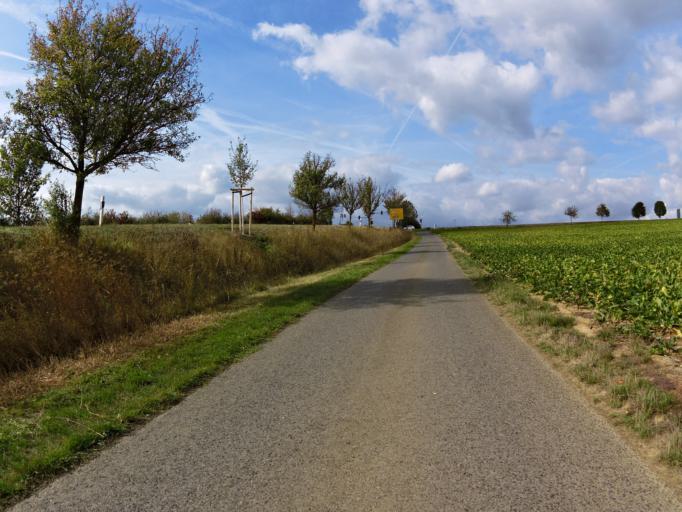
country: DE
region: Bavaria
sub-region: Regierungsbezirk Unterfranken
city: Reichenberg
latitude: 49.7319
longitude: 9.9360
